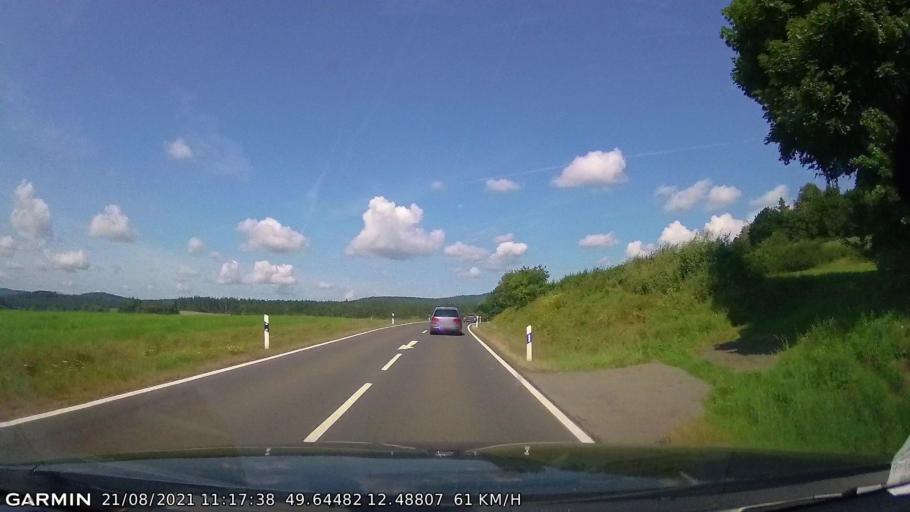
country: DE
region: Bavaria
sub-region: Upper Palatinate
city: Waidhaus
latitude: 49.6448
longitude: 12.4881
